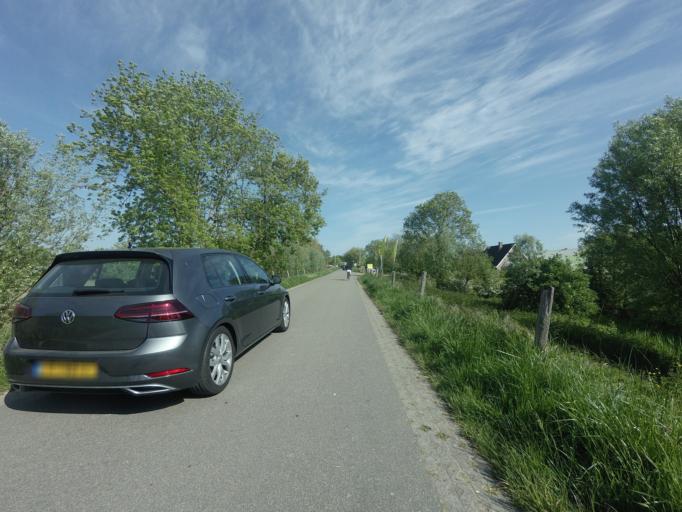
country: NL
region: Zeeland
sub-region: Gemeente Veere
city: Veere
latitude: 51.5849
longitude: 3.6060
